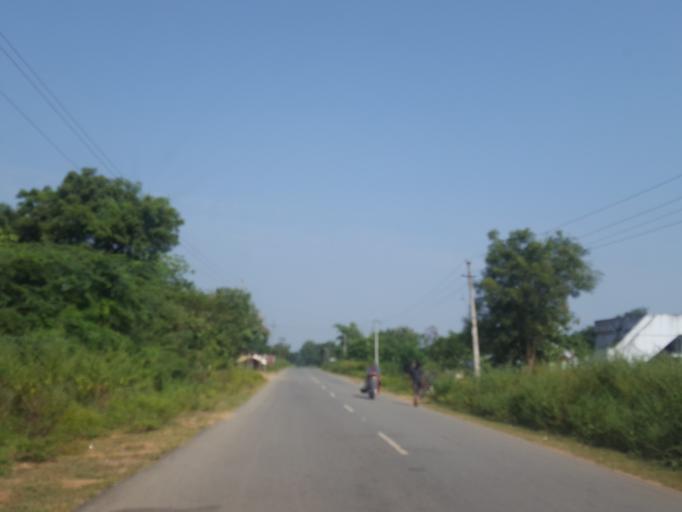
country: IN
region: Telangana
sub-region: Khammam
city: Yellandu
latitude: 17.6146
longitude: 80.3104
